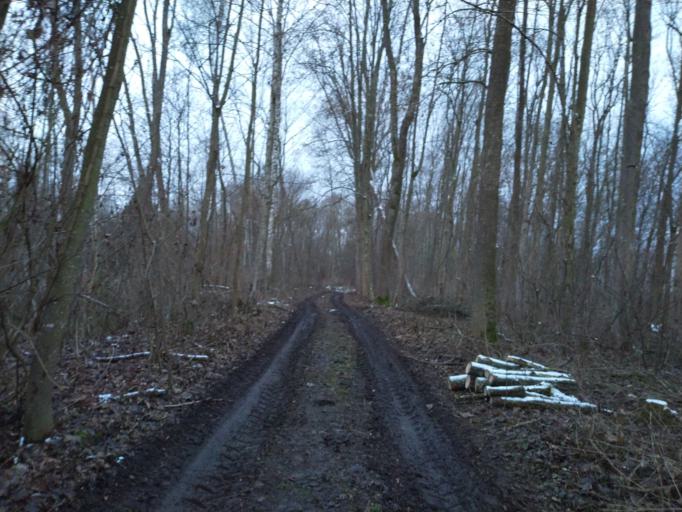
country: DE
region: Bavaria
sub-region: Swabia
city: Rettenbach
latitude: 48.4801
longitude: 10.3160
